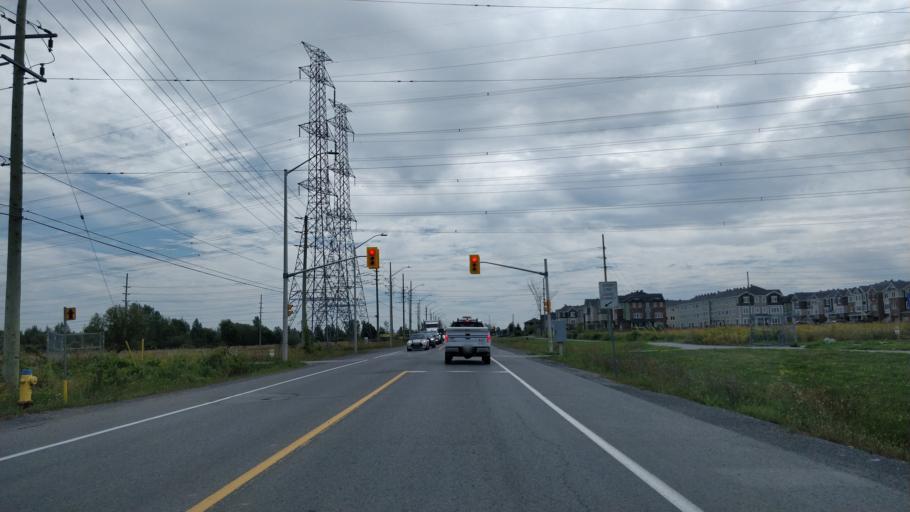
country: CA
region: Ontario
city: Bells Corners
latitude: 45.2826
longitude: -75.8828
